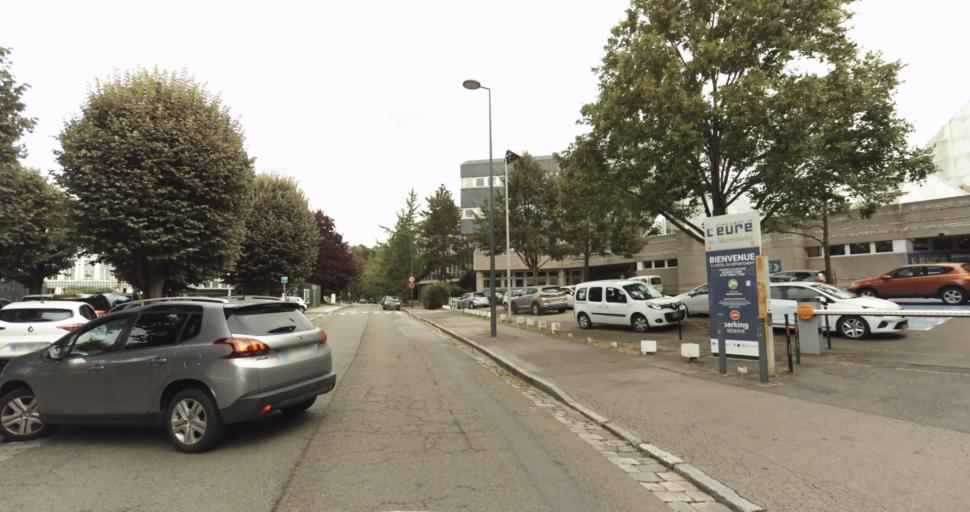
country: FR
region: Haute-Normandie
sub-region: Departement de l'Eure
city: Evreux
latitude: 49.0248
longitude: 1.1434
